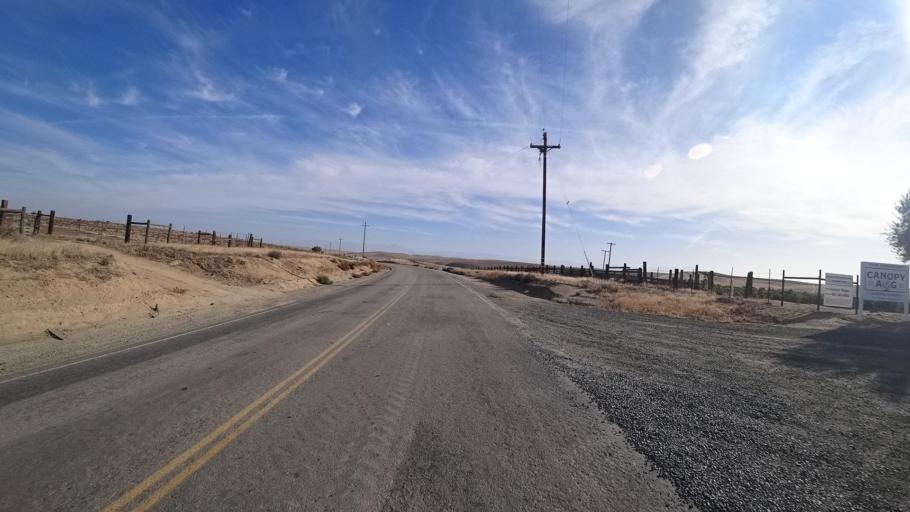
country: US
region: California
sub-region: Kern County
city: McFarland
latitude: 35.6026
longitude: -119.0724
